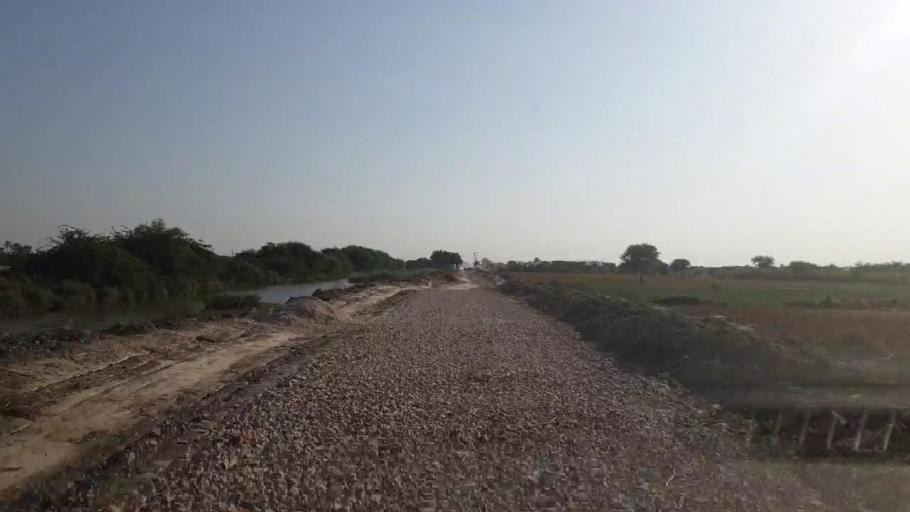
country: PK
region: Sindh
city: Talhar
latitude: 24.9272
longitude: 68.7481
